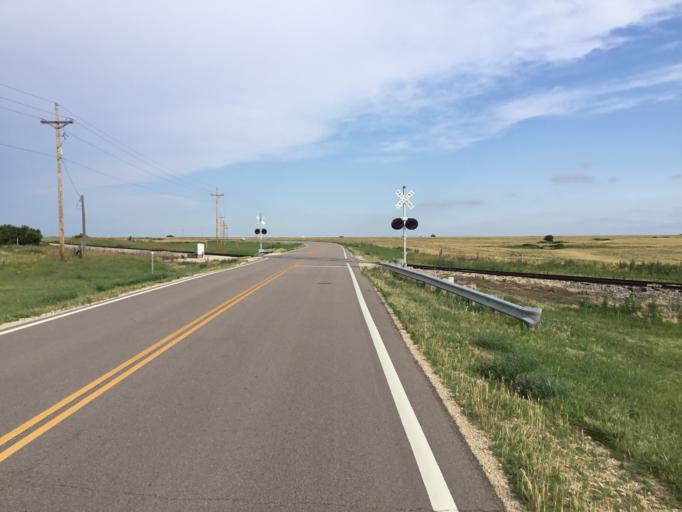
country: US
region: Kansas
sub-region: Barber County
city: Medicine Lodge
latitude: 37.4432
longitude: -98.3465
